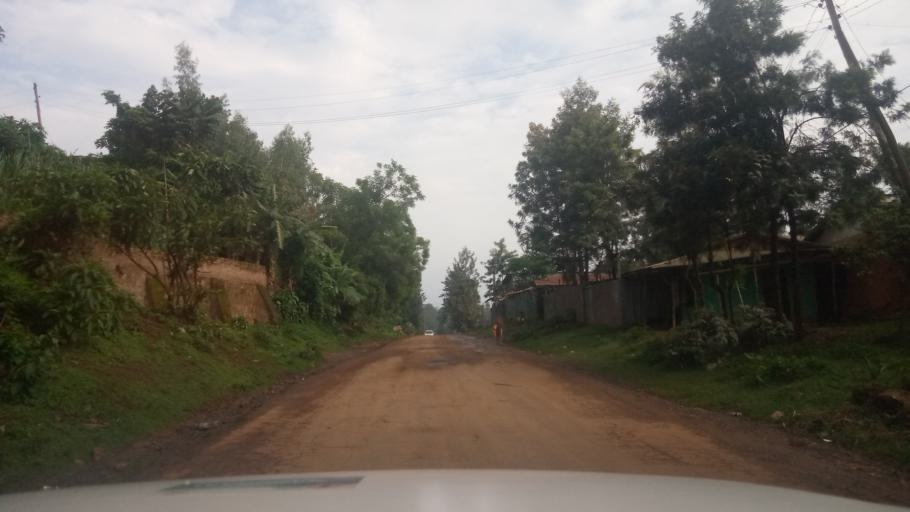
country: ET
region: Oromiya
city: Agaro
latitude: 7.8407
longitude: 36.6628
